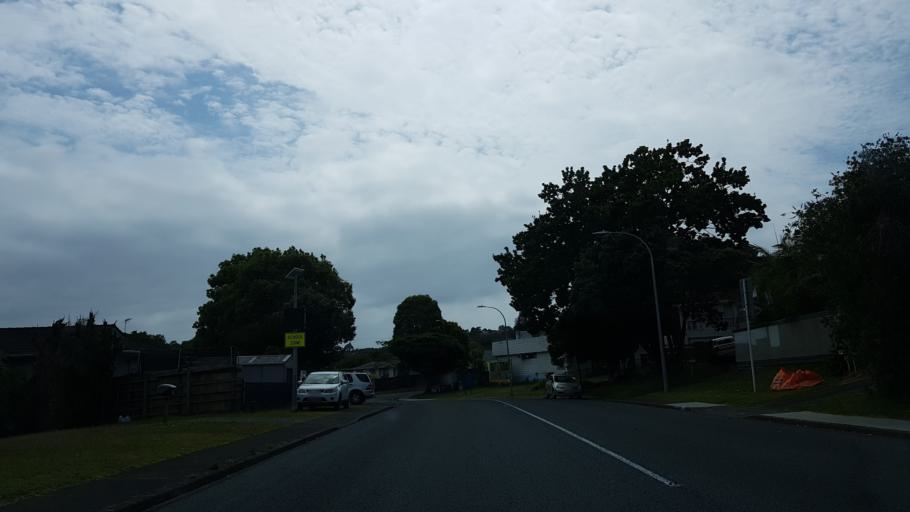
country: NZ
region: Auckland
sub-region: Auckland
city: North Shore
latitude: -36.7719
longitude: 174.7043
